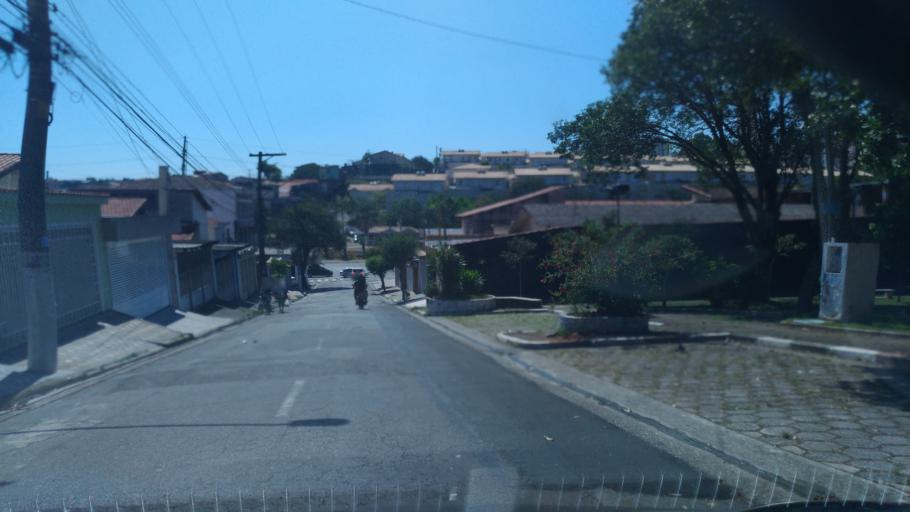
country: BR
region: Sao Paulo
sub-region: Sao Bernardo Do Campo
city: Sao Bernardo do Campo
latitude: -23.7051
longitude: -46.5773
